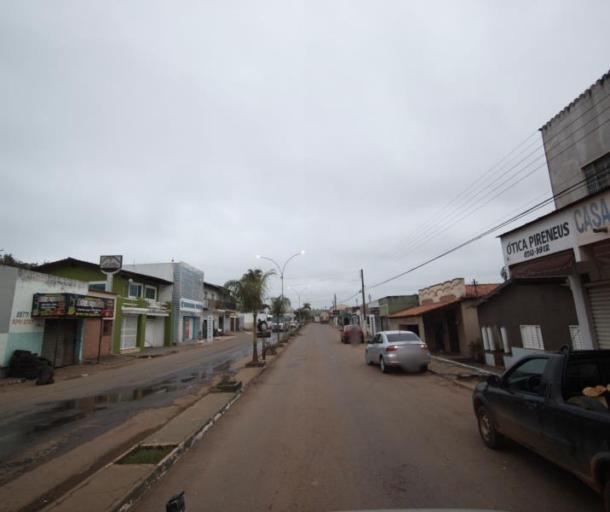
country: BR
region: Goias
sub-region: Pirenopolis
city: Pirenopolis
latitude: -15.9264
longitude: -48.8057
